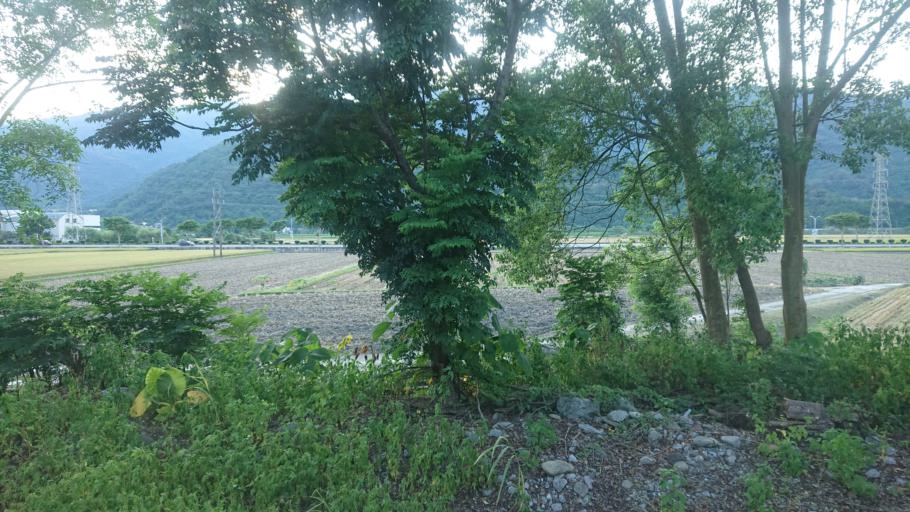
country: TW
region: Taiwan
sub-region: Taitung
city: Taitung
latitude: 23.1790
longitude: 121.2481
